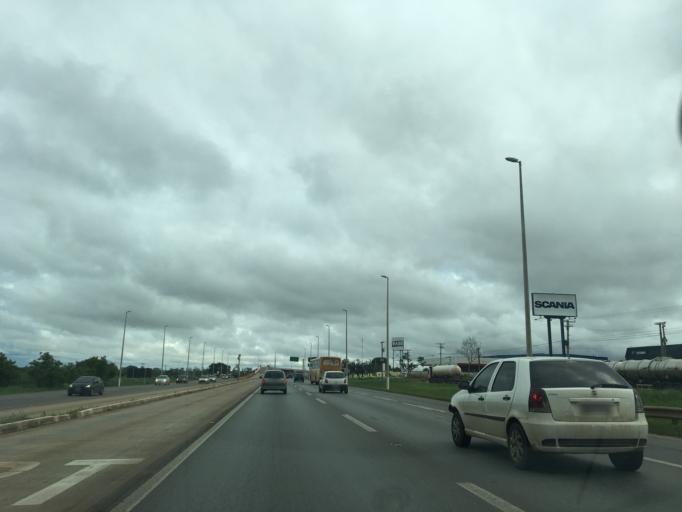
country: BR
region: Federal District
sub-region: Brasilia
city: Brasilia
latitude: -15.9953
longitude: -47.9857
